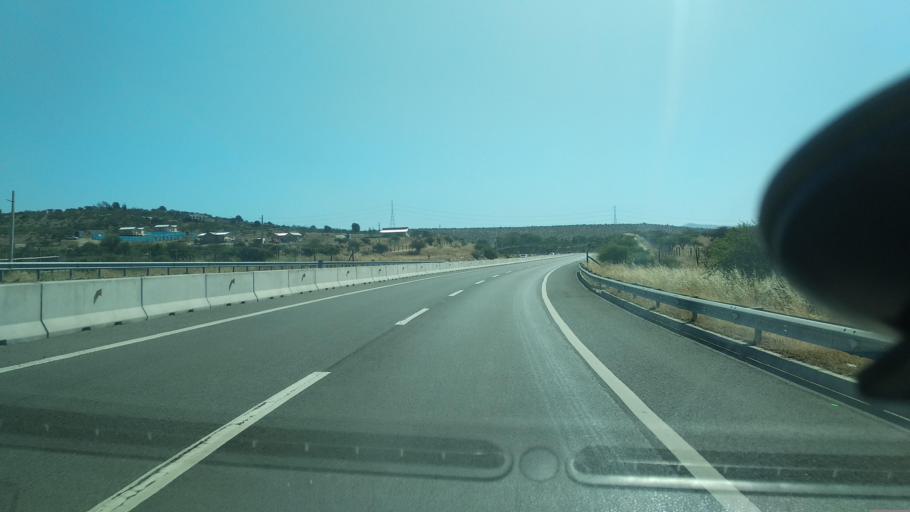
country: CL
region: Valparaiso
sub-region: Provincia de Marga Marga
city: Limache
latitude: -32.9865
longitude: -71.3202
